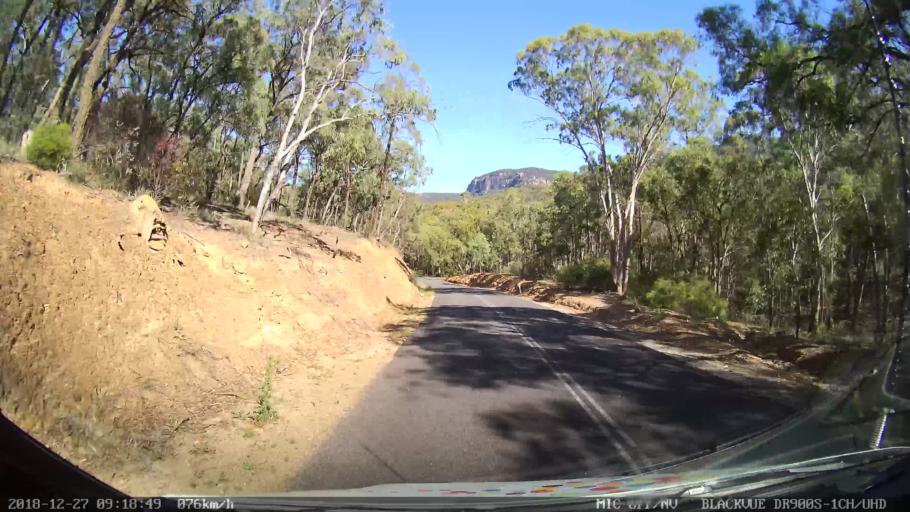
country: AU
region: New South Wales
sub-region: Lithgow
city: Portland
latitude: -33.1233
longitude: 150.0436
